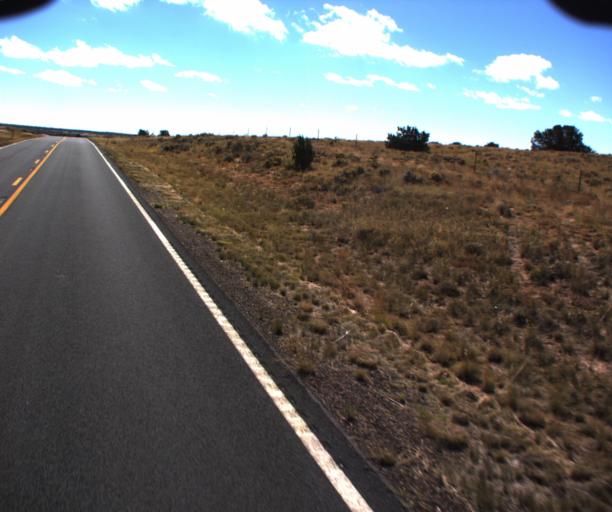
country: US
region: Arizona
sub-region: Apache County
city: Houck
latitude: 35.0116
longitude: -109.2339
